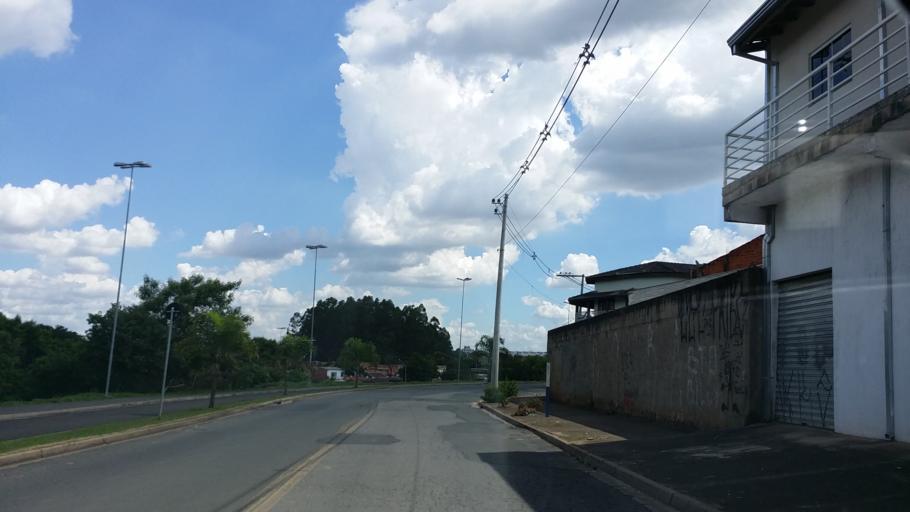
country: BR
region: Sao Paulo
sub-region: Indaiatuba
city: Indaiatuba
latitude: -23.1291
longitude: -47.2344
